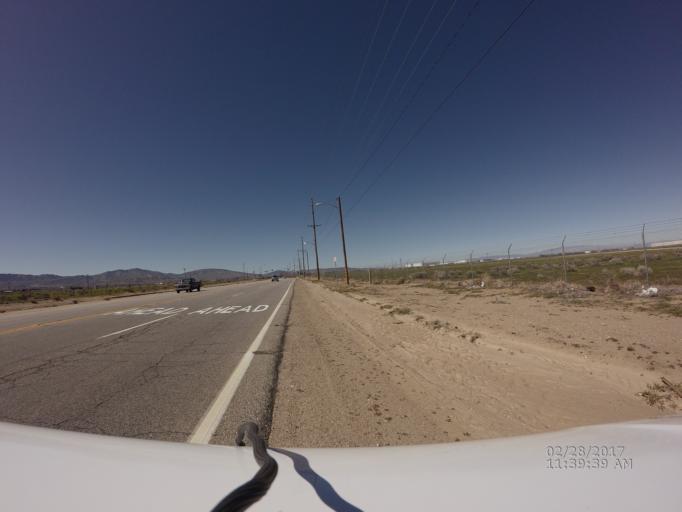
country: US
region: California
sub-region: Los Angeles County
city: Palmdale
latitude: 34.6025
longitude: -118.0921
